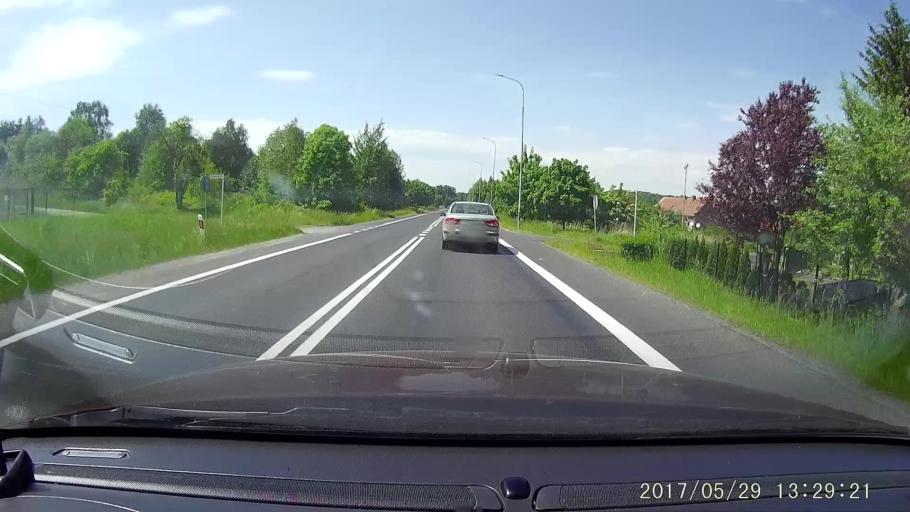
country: PL
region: Lower Silesian Voivodeship
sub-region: Powiat lubanski
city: Olszyna
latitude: 51.0698
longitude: 15.3643
